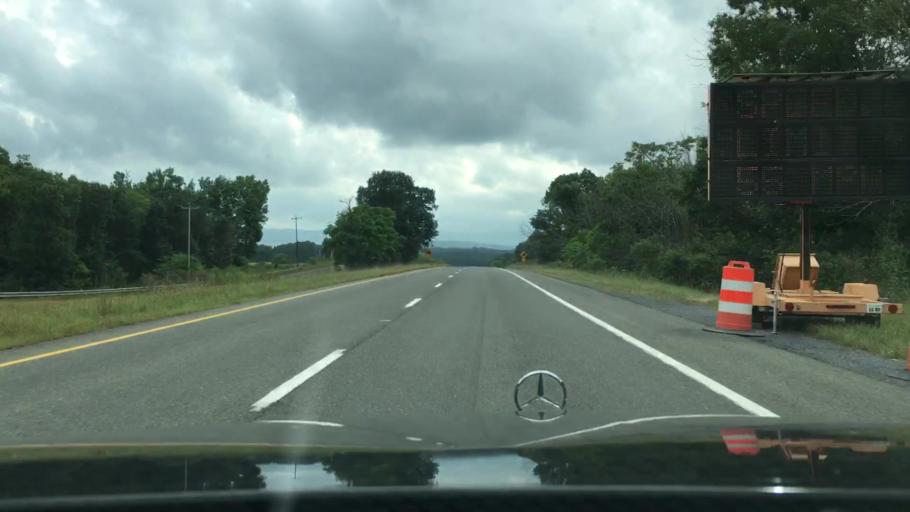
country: US
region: Virginia
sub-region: Frederick County
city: Shawnee Land
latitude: 39.3596
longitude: -78.3042
